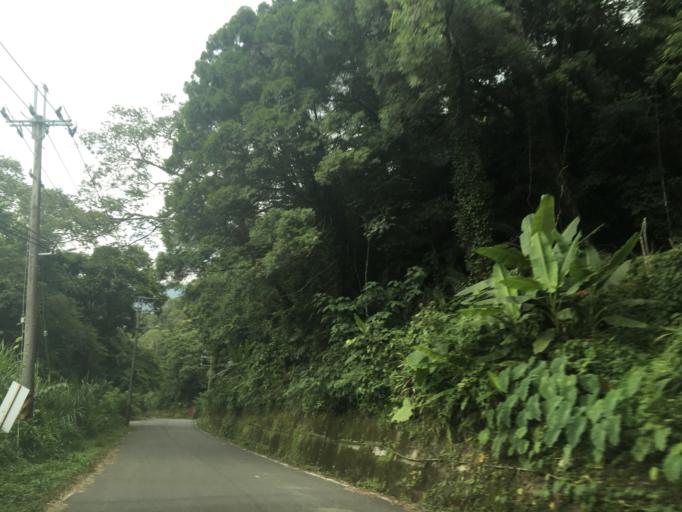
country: TW
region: Taiwan
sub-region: Miaoli
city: Miaoli
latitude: 24.3487
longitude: 120.9449
